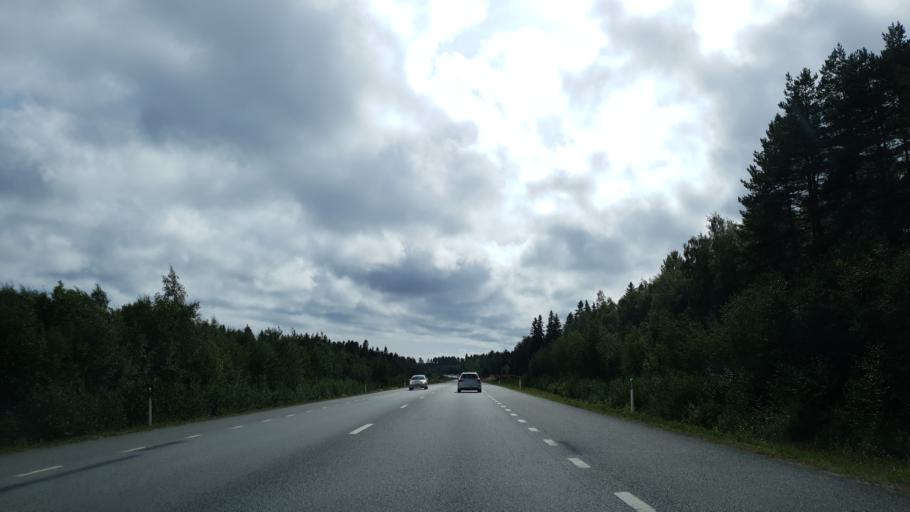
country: SE
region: Vaesterbotten
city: Obbola
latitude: 63.7461
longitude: 20.2926
